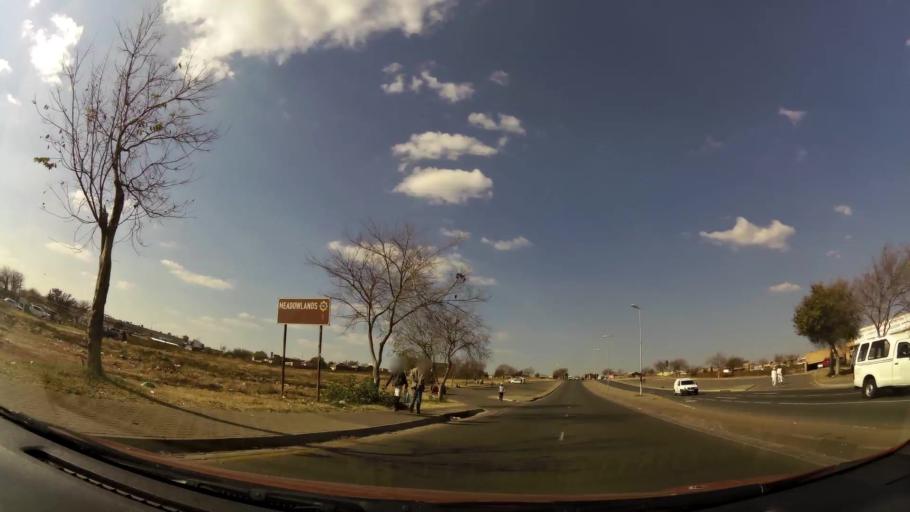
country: ZA
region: Gauteng
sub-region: City of Johannesburg Metropolitan Municipality
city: Roodepoort
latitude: -26.2144
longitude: 27.8840
